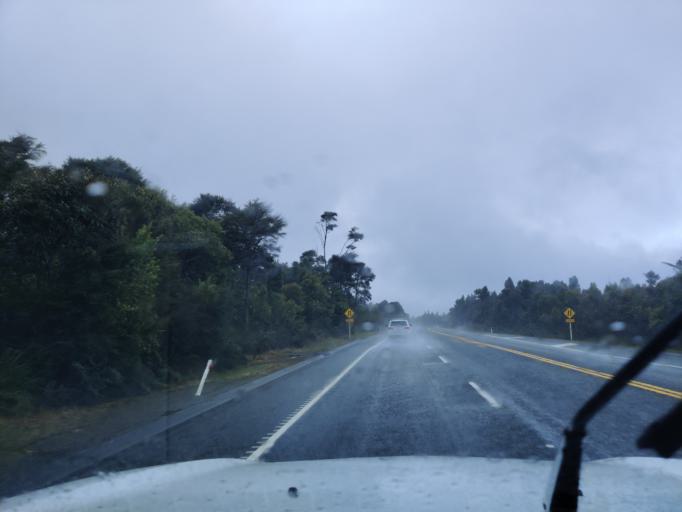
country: NZ
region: Waikato
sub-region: South Waikato District
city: Tokoroa
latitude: -38.0148
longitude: 175.9469
